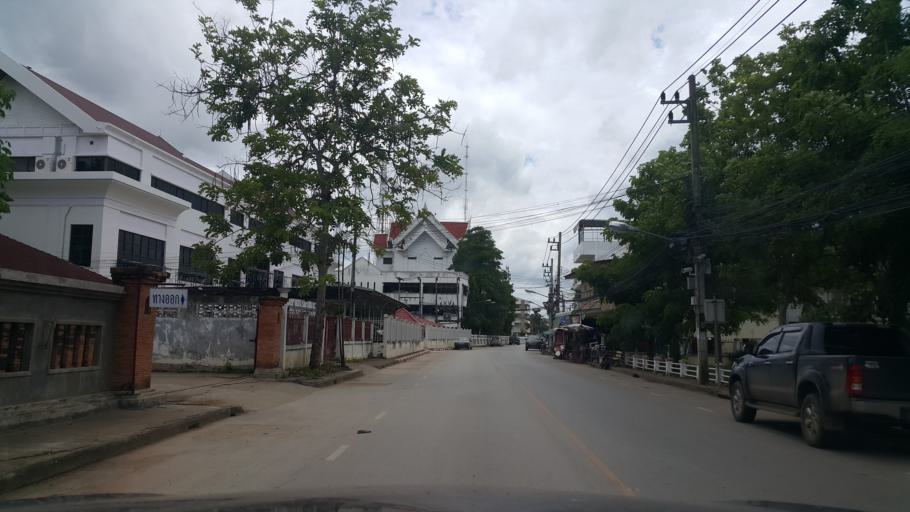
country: TH
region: Sukhothai
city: Sukhothai
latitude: 17.0054
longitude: 99.8286
